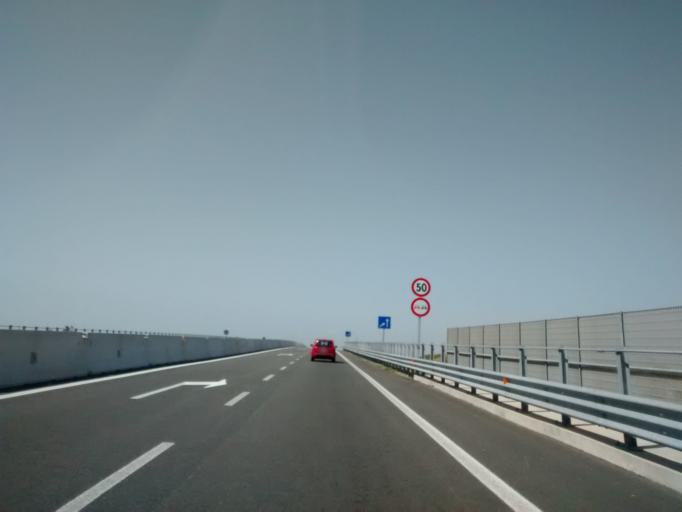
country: IT
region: Sardinia
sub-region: Provincia di Cagliari
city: Quartu Sant'Elena
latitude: 39.2581
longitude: 9.2619
